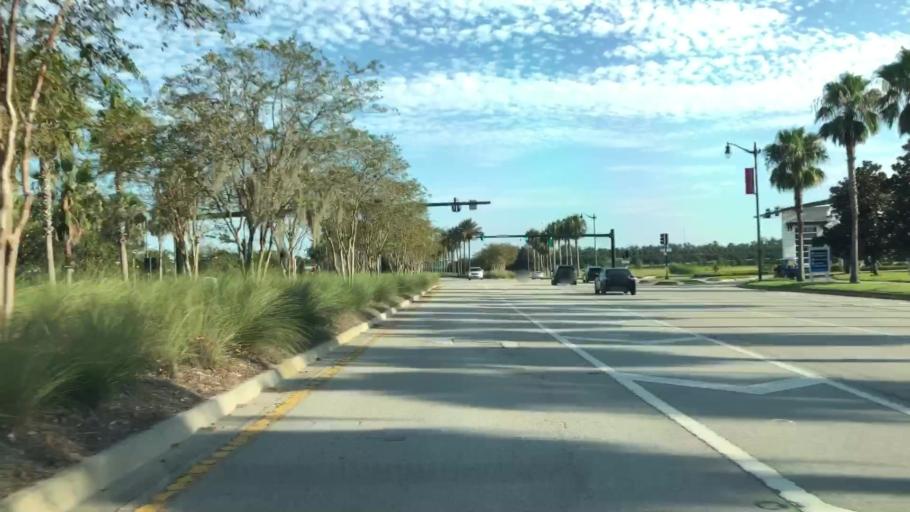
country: US
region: Florida
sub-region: Saint Johns County
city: Palm Valley
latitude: 30.1082
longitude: -81.4161
